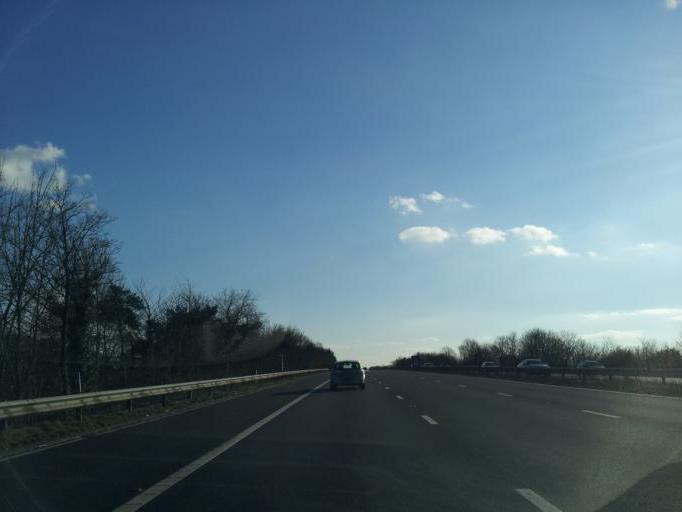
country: GB
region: England
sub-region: Devon
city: Uffculme
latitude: 50.8981
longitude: -3.3726
